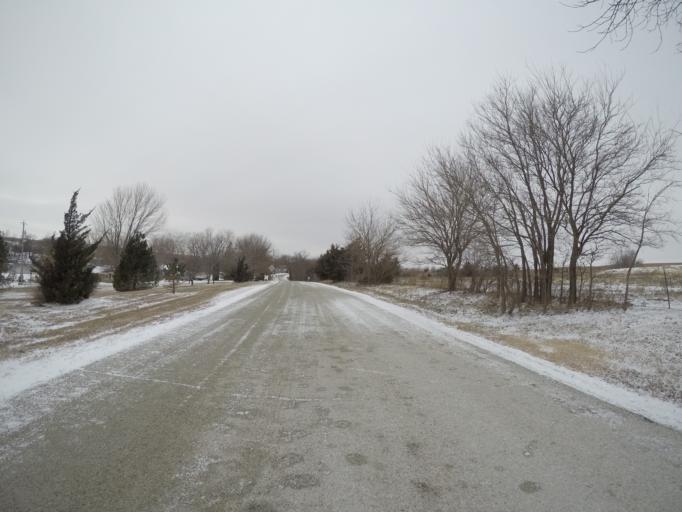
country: US
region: Kansas
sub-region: Wabaunsee County
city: Alma
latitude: 38.8557
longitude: -96.1875
